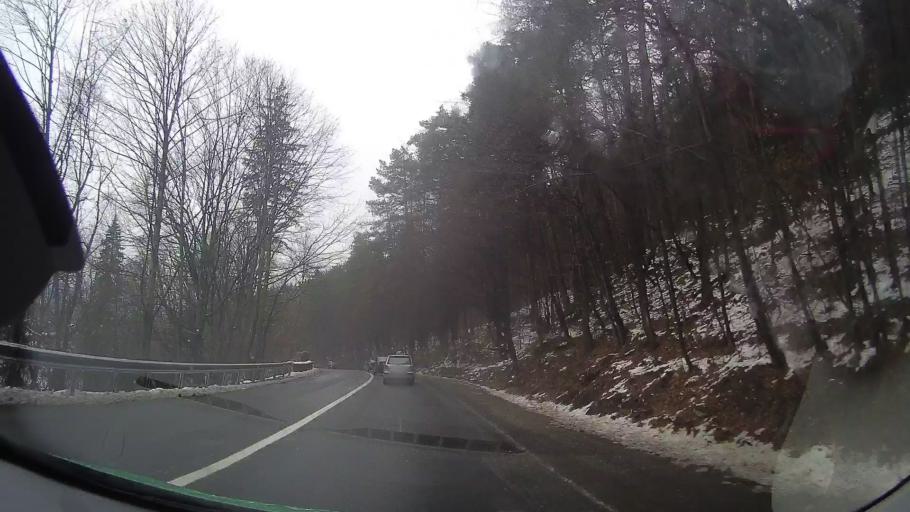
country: RO
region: Neamt
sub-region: Comuna Tarcau
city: Tarcau
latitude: 46.8950
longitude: 26.1231
